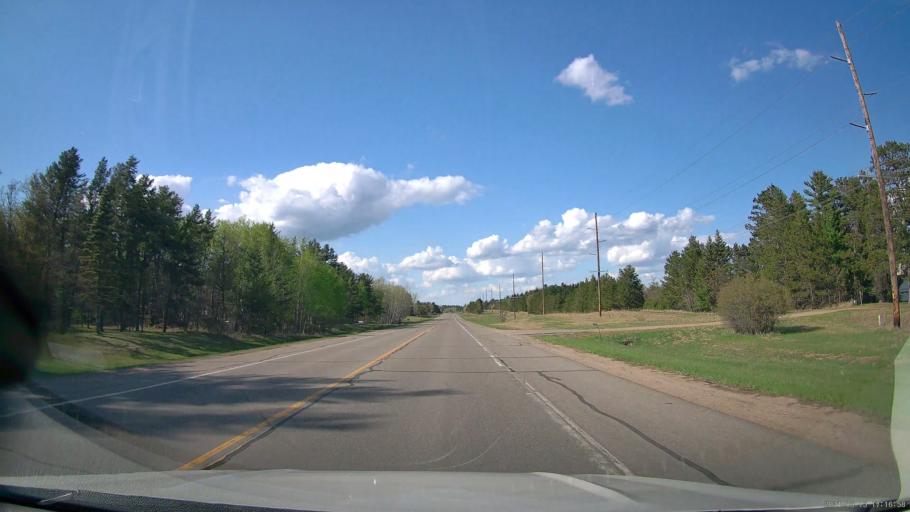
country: US
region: Minnesota
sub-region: Hubbard County
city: Park Rapids
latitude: 46.9369
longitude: -95.0168
